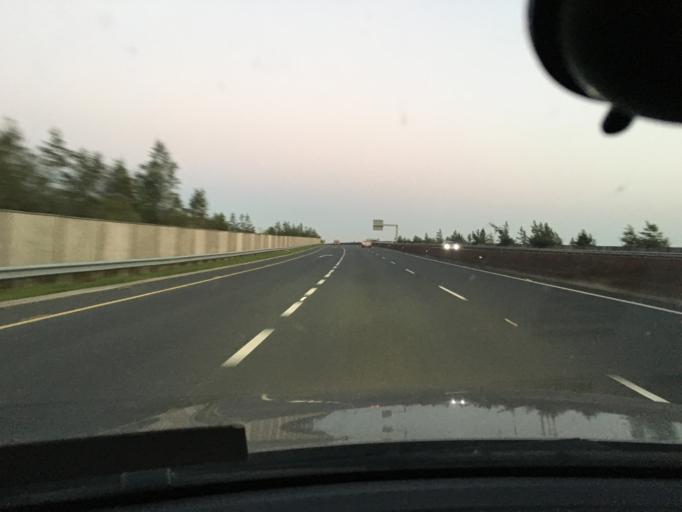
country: IE
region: Connaught
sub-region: County Galway
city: Athenry
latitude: 53.2847
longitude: -8.7553
